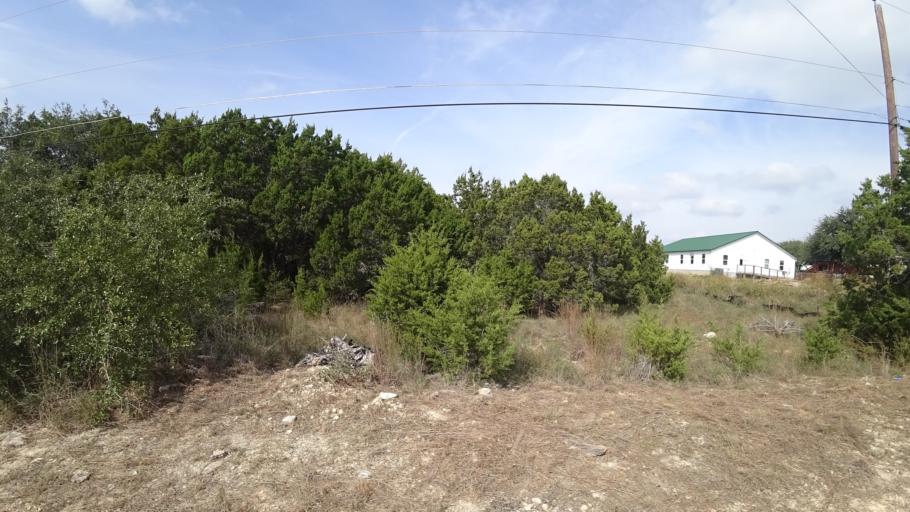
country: US
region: Texas
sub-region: Travis County
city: Hudson Bend
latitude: 30.3891
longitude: -97.9386
